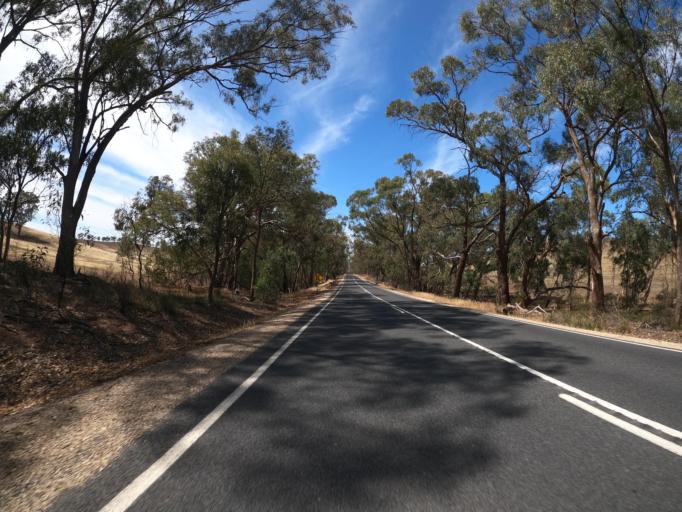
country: AU
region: Victoria
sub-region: Benalla
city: Benalla
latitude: -36.3791
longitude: 145.9763
